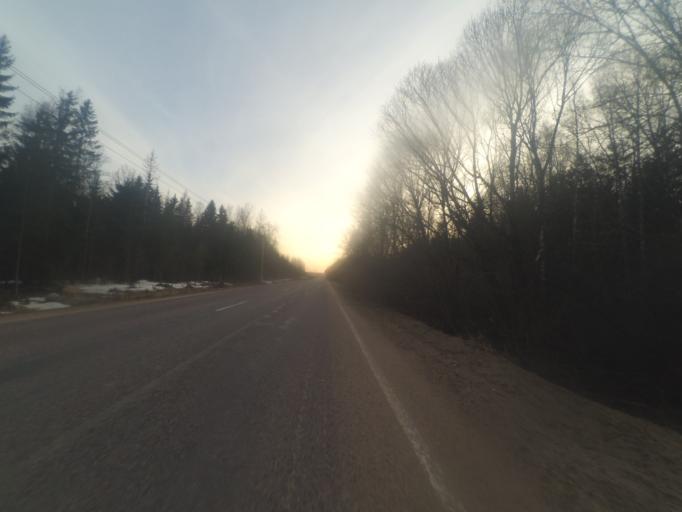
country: RU
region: Moskovskaya
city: Karinskoye
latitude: 55.7762
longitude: 36.6017
